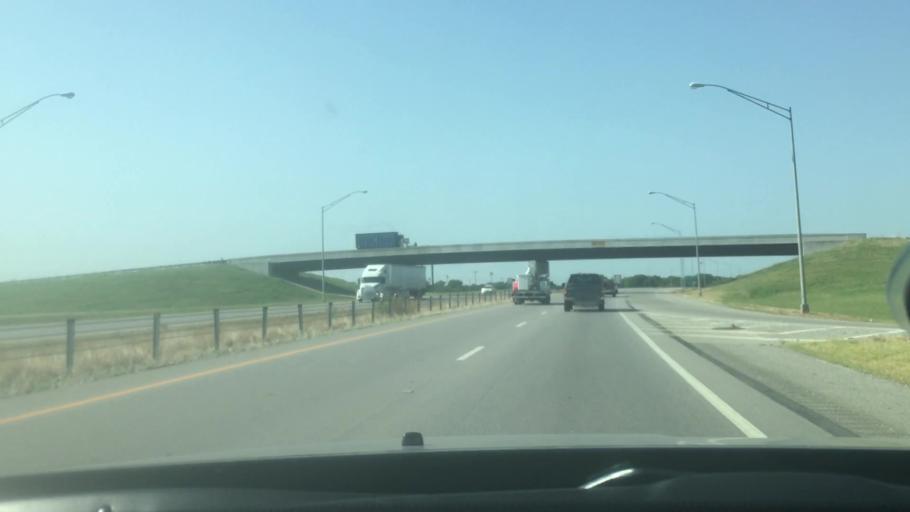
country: US
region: Oklahoma
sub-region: Bryan County
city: Calera
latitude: 33.9483
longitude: -96.4169
